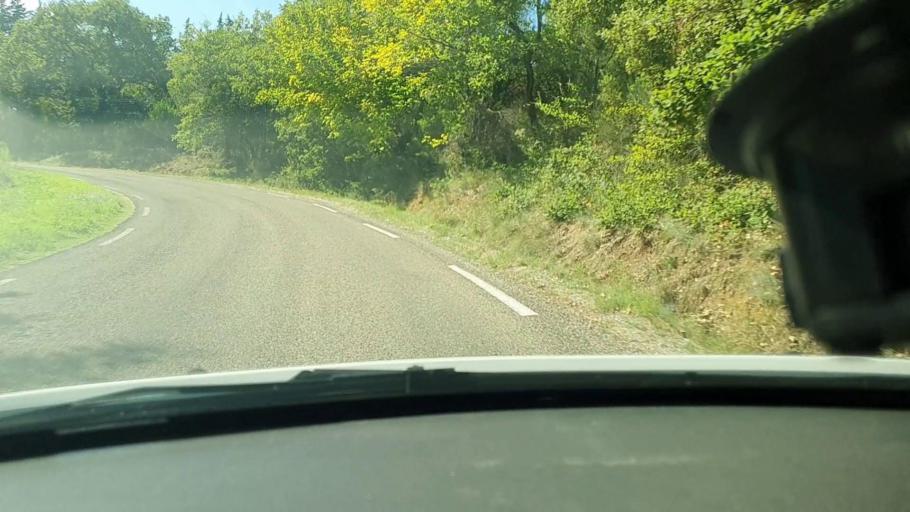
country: FR
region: Languedoc-Roussillon
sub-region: Departement du Gard
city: Goudargues
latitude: 44.1678
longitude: 4.4845
